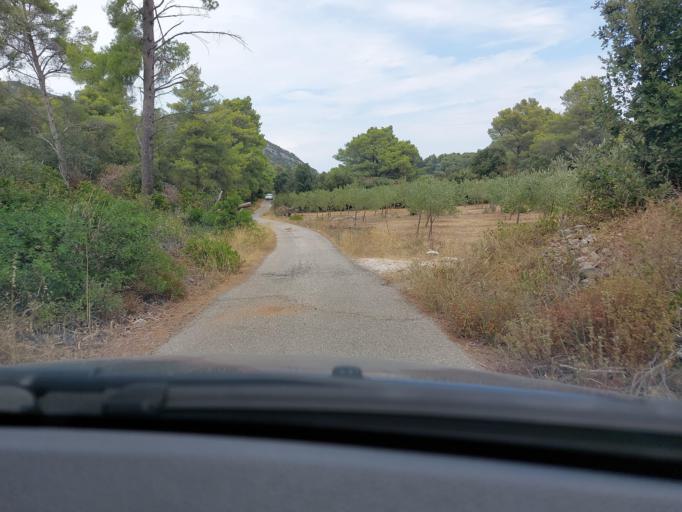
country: HR
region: Dubrovacko-Neretvanska
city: Smokvica
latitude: 42.7584
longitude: 16.9315
